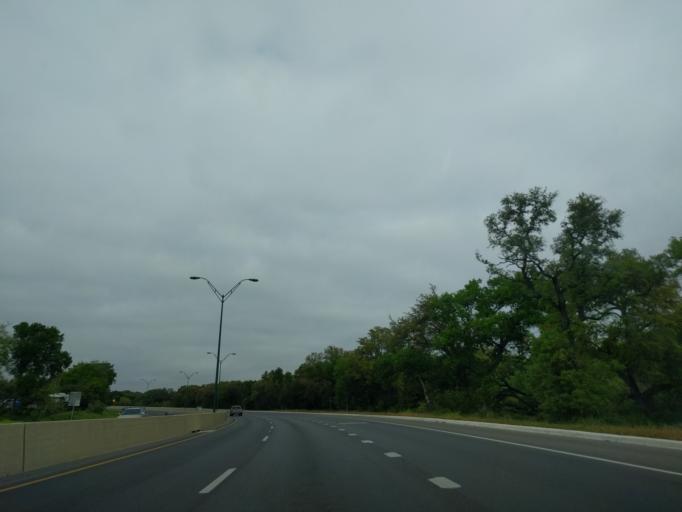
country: US
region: Texas
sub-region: Bexar County
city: Castle Hills
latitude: 29.5523
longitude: -98.4771
